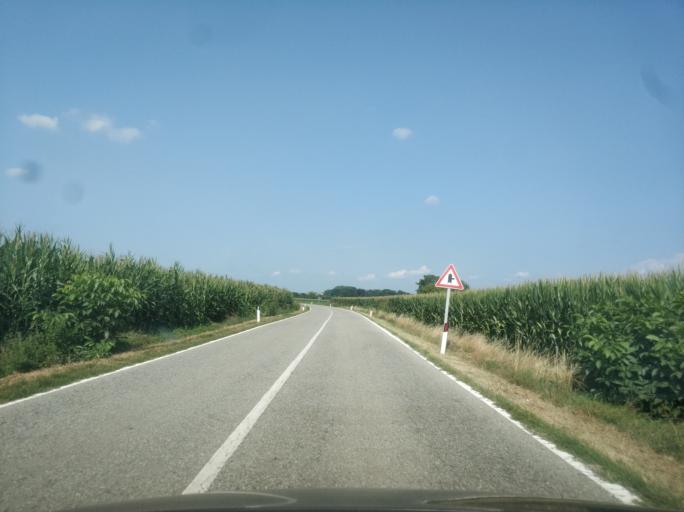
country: IT
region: Piedmont
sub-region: Provincia di Cuneo
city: Caraglio
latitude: 44.4402
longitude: 7.4513
